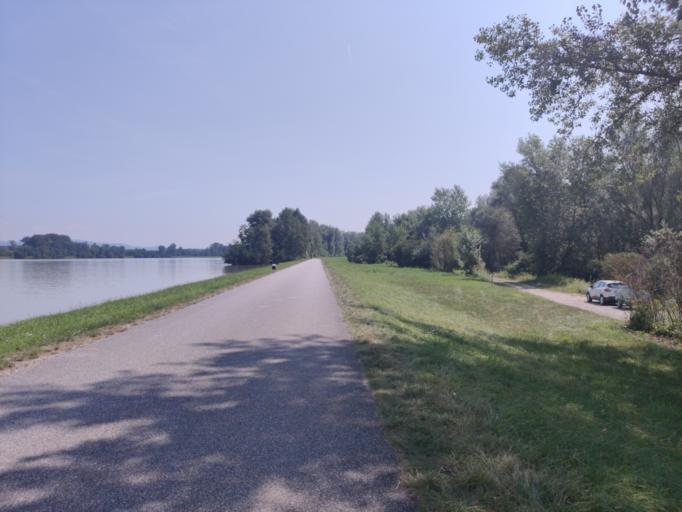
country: AT
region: Upper Austria
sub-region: Politischer Bezirk Urfahr-Umgebung
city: Feldkirchen an der Donau
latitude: 48.3245
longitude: 14.0485
